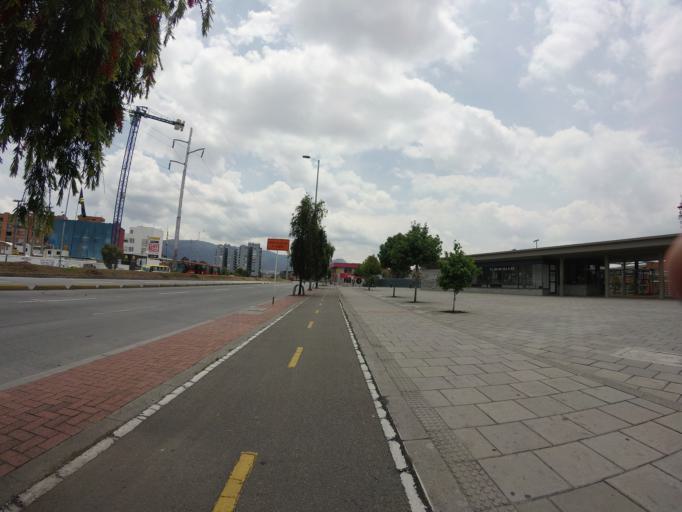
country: CO
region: Bogota D.C.
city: Barrio San Luis
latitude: 4.6976
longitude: -74.0697
